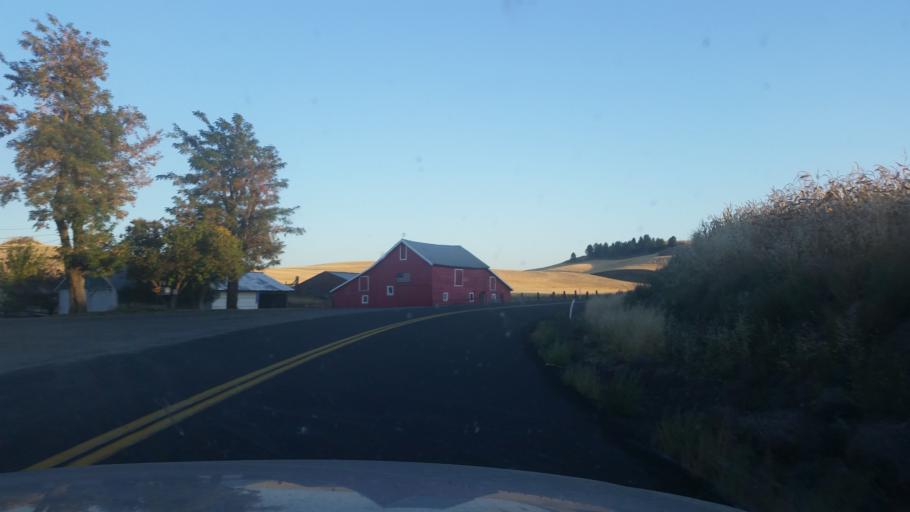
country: US
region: Washington
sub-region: Spokane County
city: Cheney
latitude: 47.5360
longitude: -117.6240
